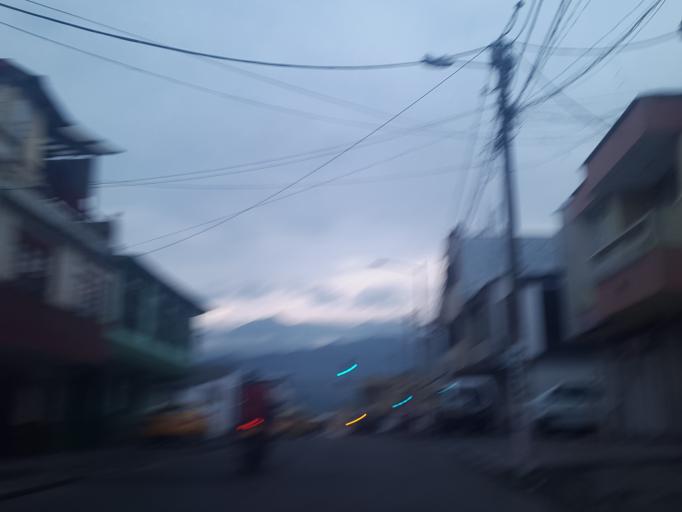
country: CO
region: Quindio
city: Armenia
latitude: 4.5389
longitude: -75.6774
